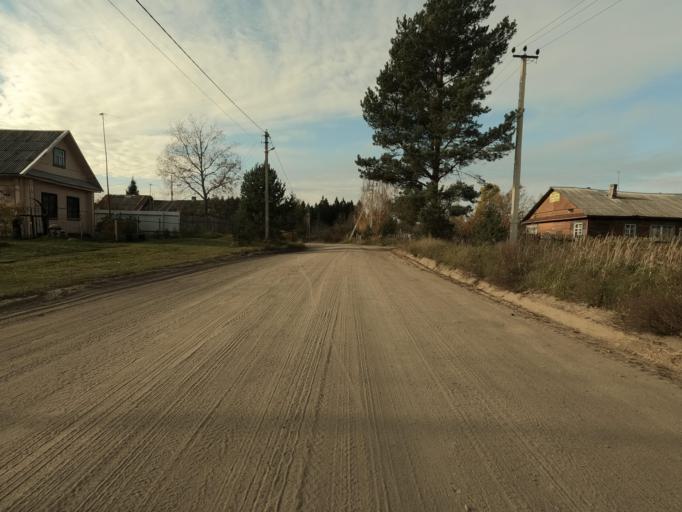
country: RU
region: Leningrad
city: Priladozhskiy
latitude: 59.6307
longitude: 31.4001
